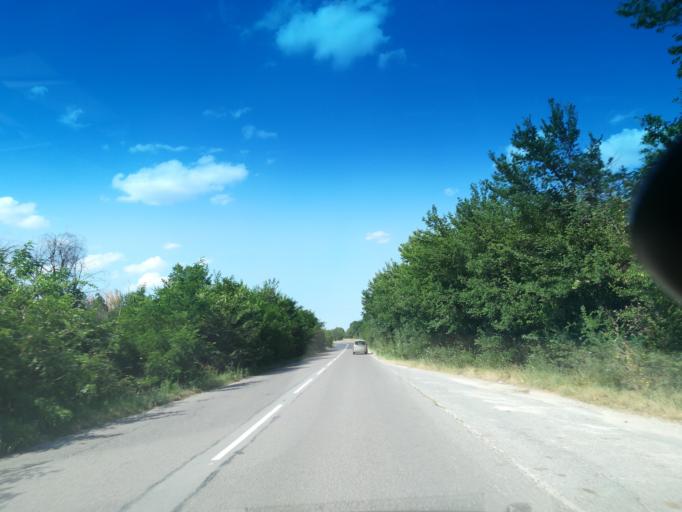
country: BG
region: Stara Zagora
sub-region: Obshtina Chirpan
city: Chirpan
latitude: 42.2453
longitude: 25.4094
